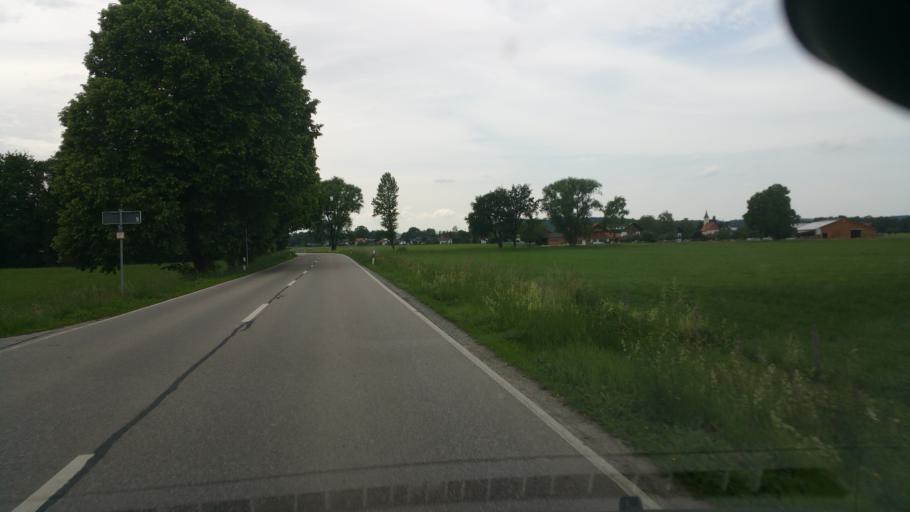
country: DE
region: Bavaria
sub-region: Upper Bavaria
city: Bruckmuhl
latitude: 47.8652
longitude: 11.9328
